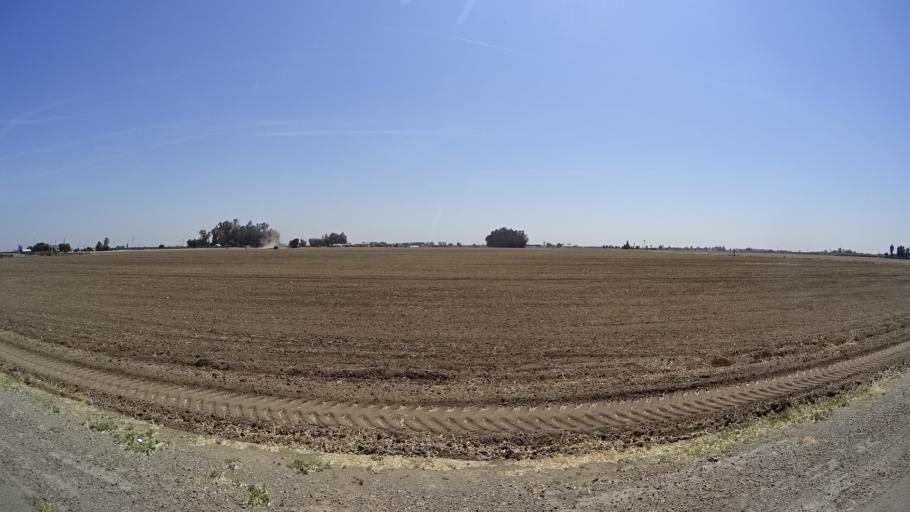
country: US
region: California
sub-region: Fresno County
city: Riverdale
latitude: 36.4067
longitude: -119.8513
